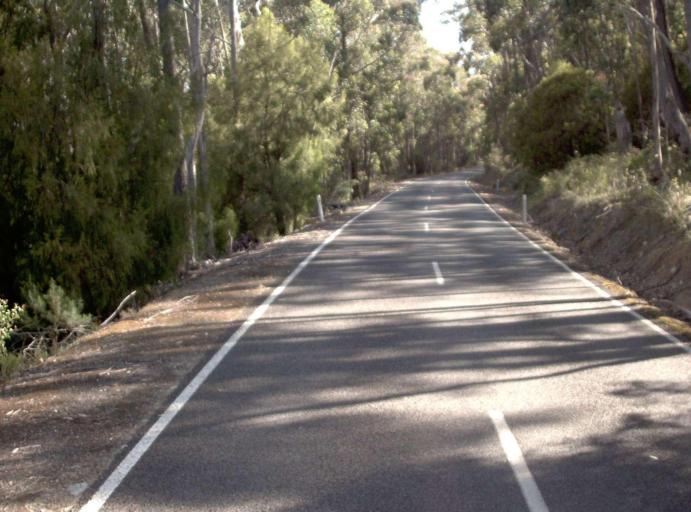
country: AU
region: Victoria
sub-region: East Gippsland
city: Lakes Entrance
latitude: -37.6045
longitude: 148.5231
